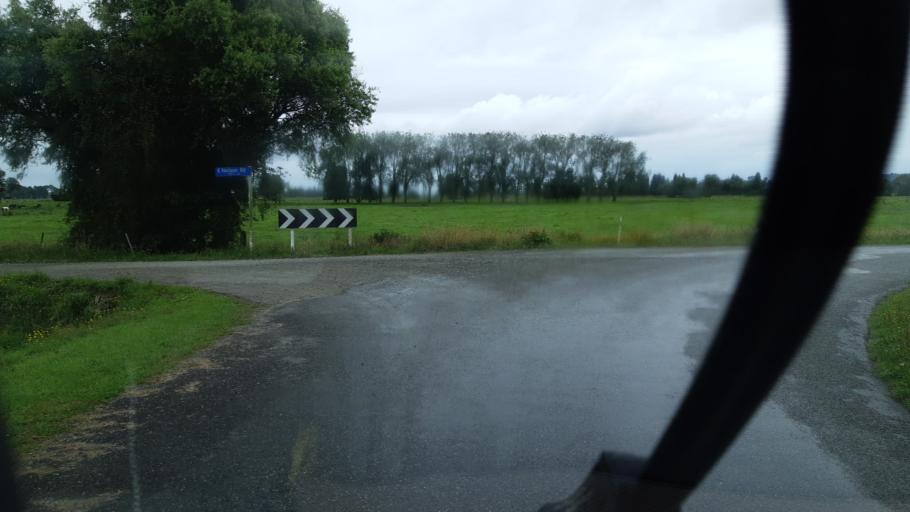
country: NZ
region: West Coast
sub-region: Westland District
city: Hokitika
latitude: -42.8826
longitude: 171.0300
